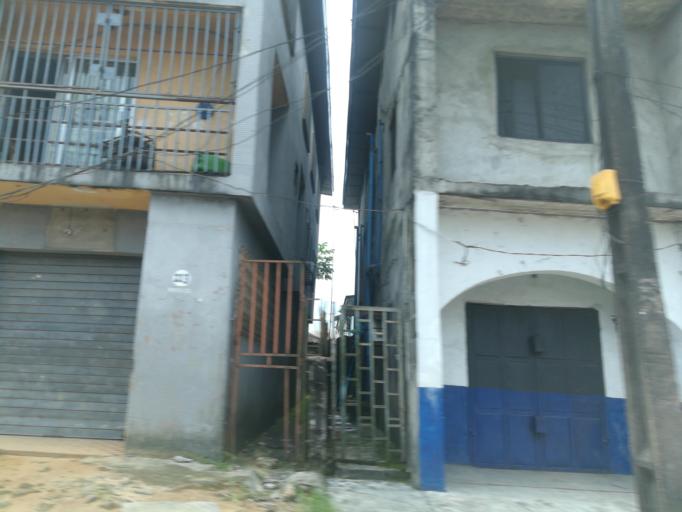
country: NG
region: Rivers
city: Port Harcourt
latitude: 4.7599
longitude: 7.0323
